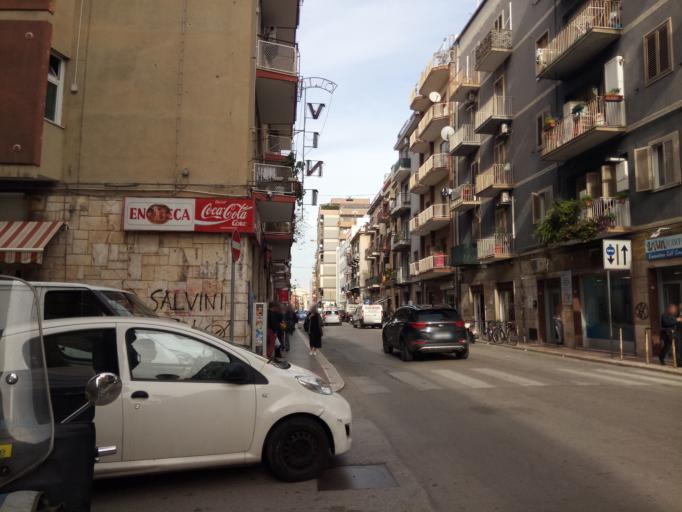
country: IT
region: Apulia
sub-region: Provincia di Bari
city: Bari
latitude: 41.1092
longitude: 16.8677
